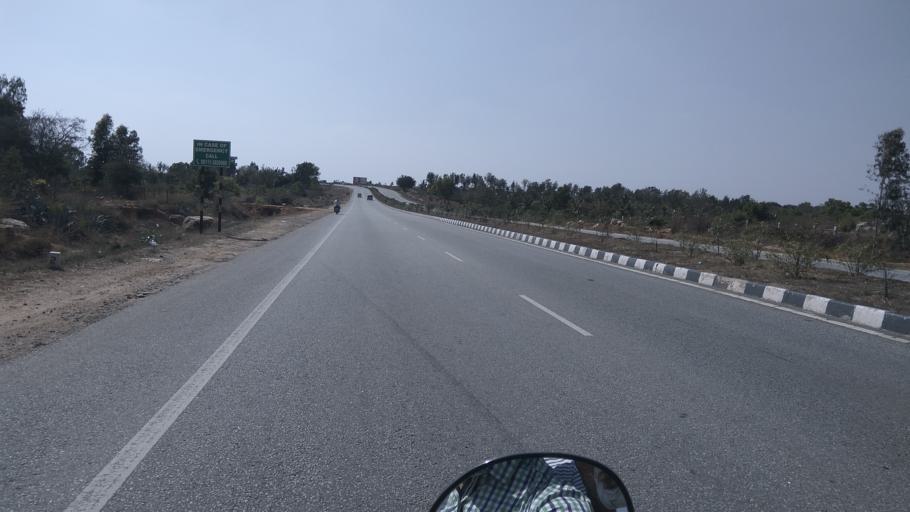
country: IN
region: Karnataka
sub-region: Kolar
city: Mulbagal
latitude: 13.1527
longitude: 78.3129
